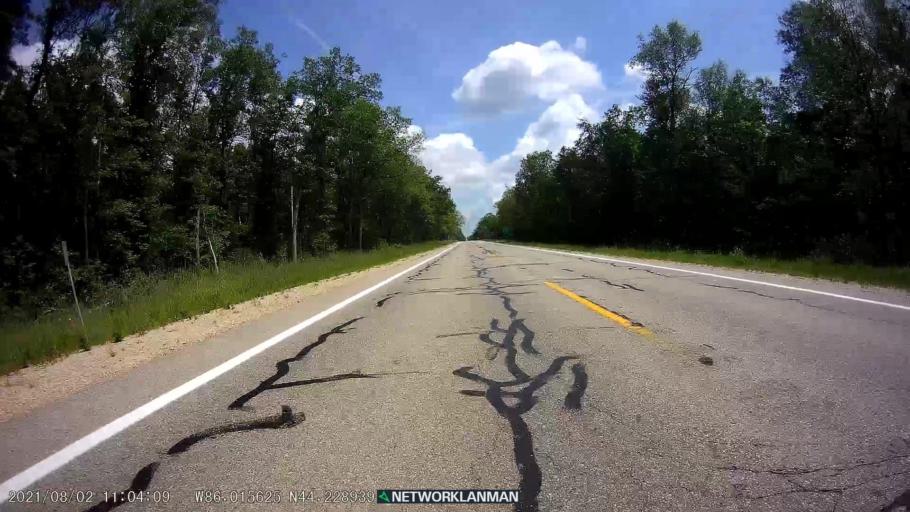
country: US
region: Michigan
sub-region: Manistee County
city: Manistee
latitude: 44.2290
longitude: -86.0159
